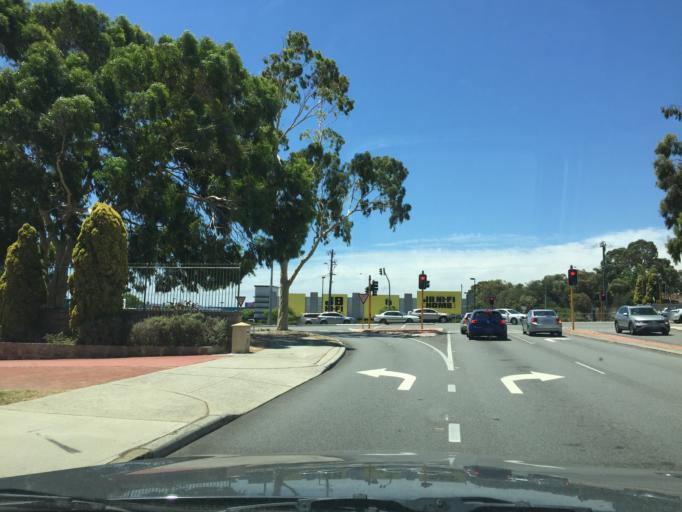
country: AU
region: Western Australia
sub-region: Melville
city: Winthrop
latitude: -32.0467
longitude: 115.8257
